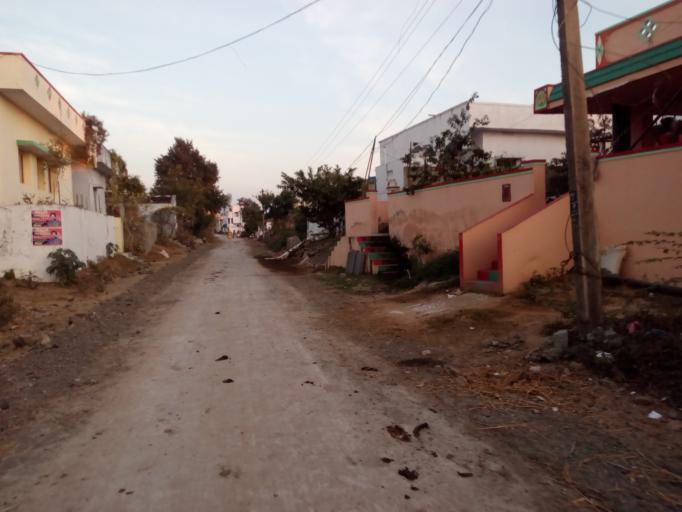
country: IN
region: Andhra Pradesh
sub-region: Prakasam
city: Vetapalem
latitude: 15.7281
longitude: 80.2505
